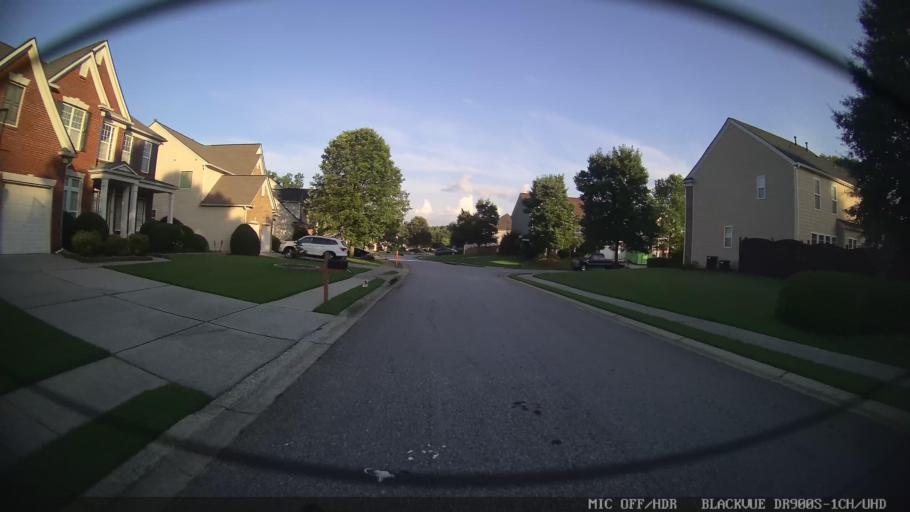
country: US
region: Georgia
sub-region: Forsyth County
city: Cumming
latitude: 34.2181
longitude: -84.2332
